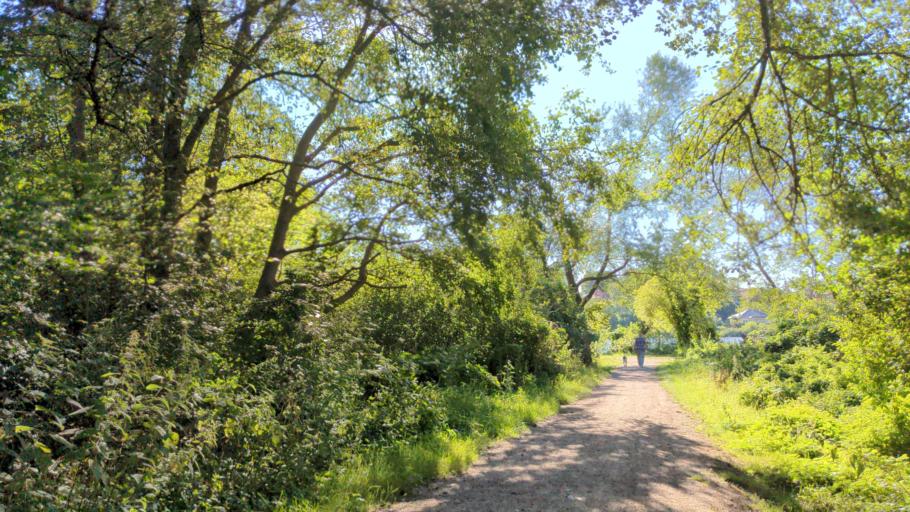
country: DE
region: Mecklenburg-Vorpommern
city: Selmsdorf
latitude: 53.8469
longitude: 10.9281
